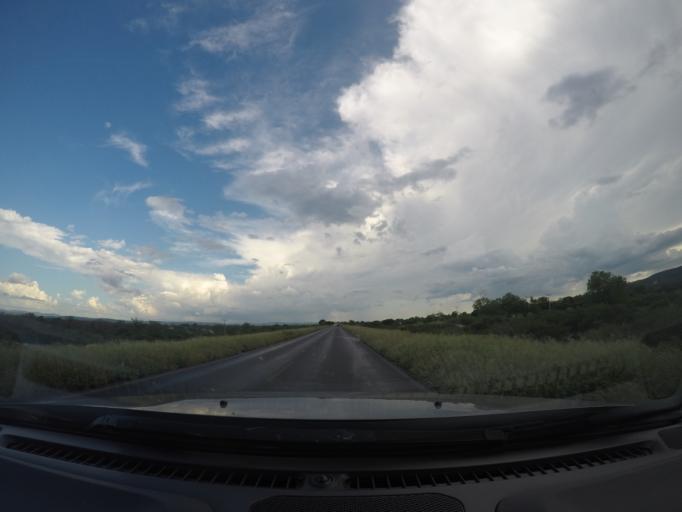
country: BR
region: Bahia
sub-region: Ibotirama
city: Ibotirama
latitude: -12.1475
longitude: -43.3140
